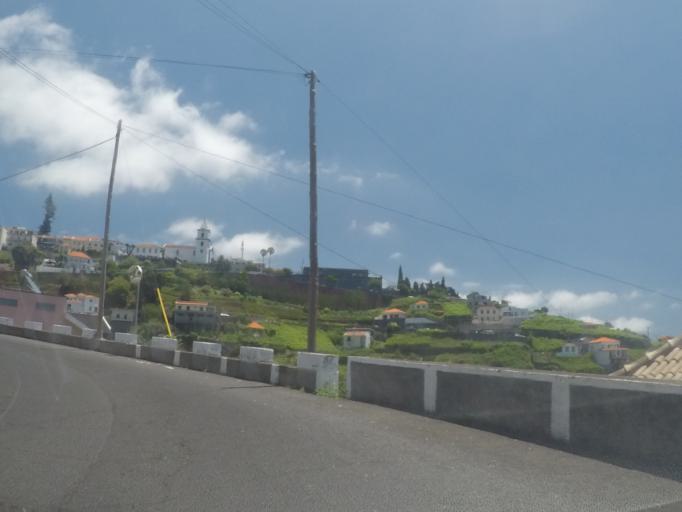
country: PT
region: Madeira
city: Camara de Lobos
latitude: 32.6702
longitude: -16.9837
